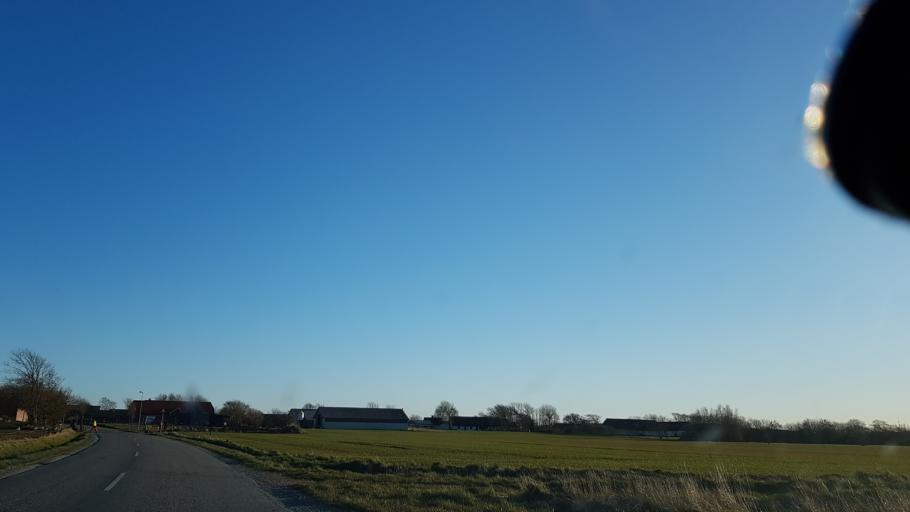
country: DK
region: South Denmark
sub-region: Esbjerg Kommune
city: Bramming
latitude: 55.4006
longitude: 8.7021
